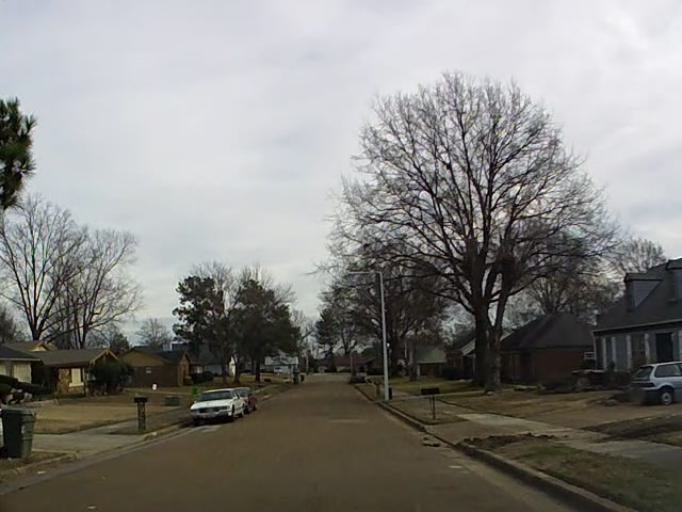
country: US
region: Tennessee
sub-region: Shelby County
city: Germantown
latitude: 35.0542
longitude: -89.8453
